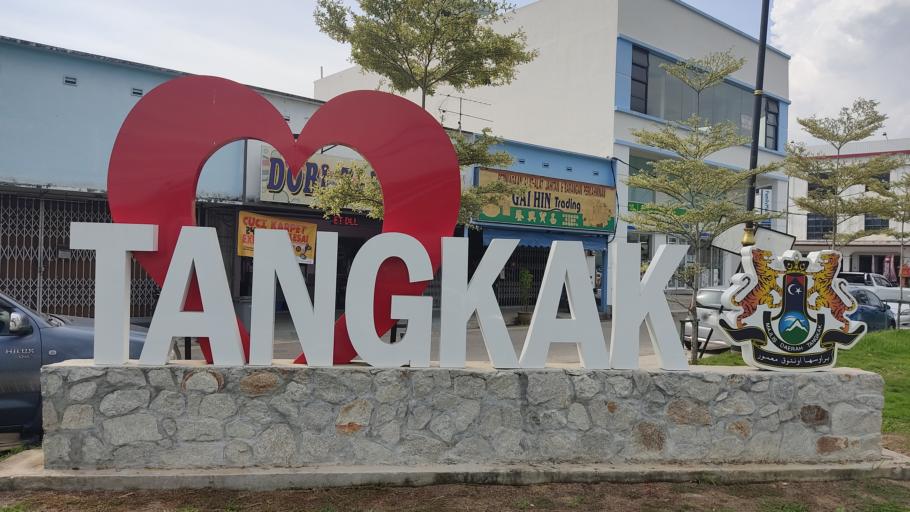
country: MY
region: Johor
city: Tangkak
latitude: 2.2620
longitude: 102.5367
